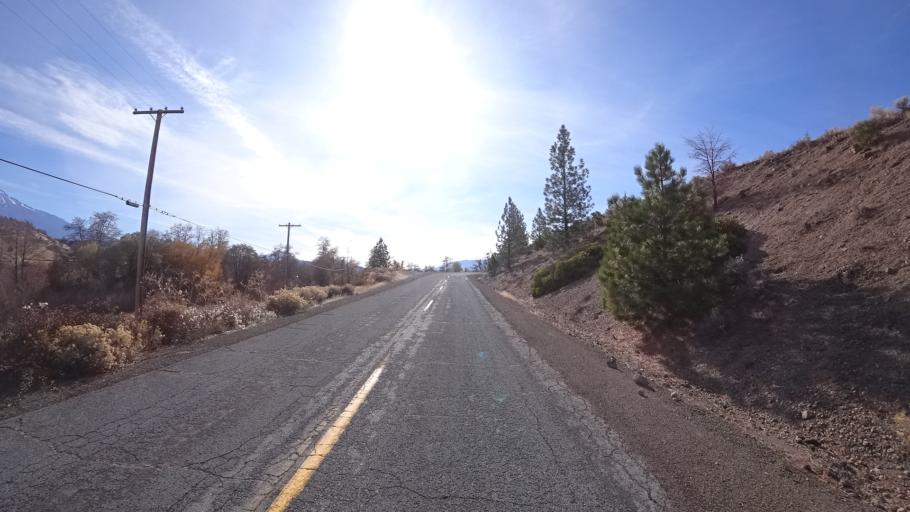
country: US
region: California
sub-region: Siskiyou County
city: Weed
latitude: 41.4735
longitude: -122.4406
